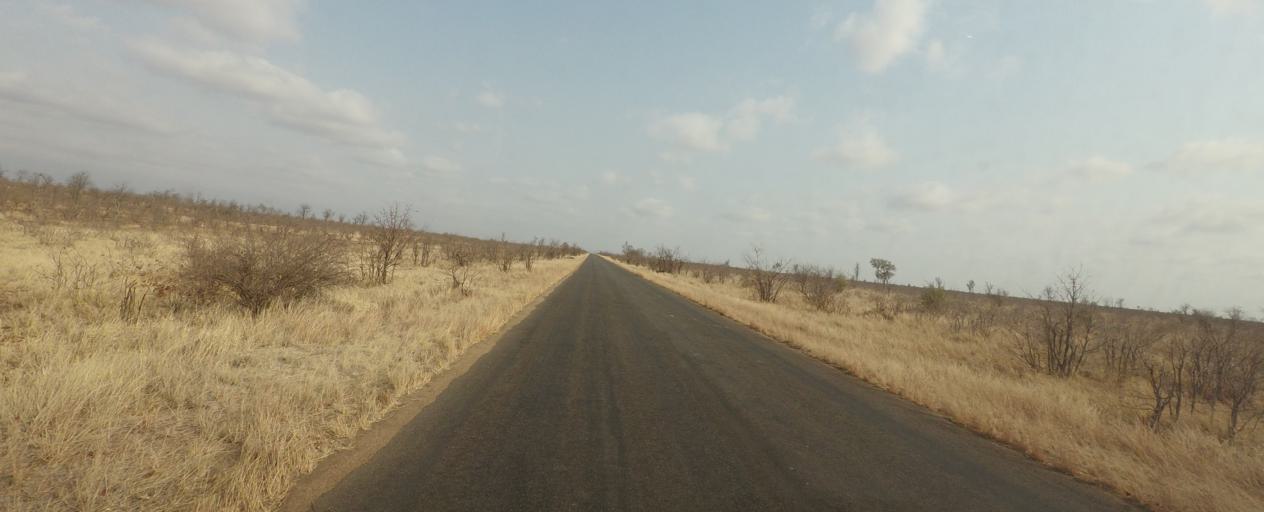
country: ZA
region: Limpopo
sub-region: Vhembe District Municipality
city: Mutale
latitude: -22.9257
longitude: 31.2596
